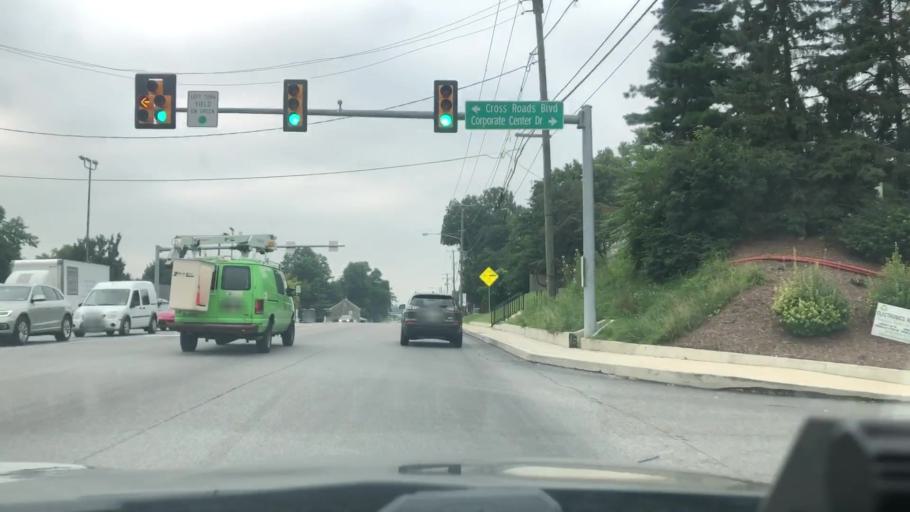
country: US
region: Pennsylvania
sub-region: Berks County
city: Temple
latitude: 40.4090
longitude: -75.9379
